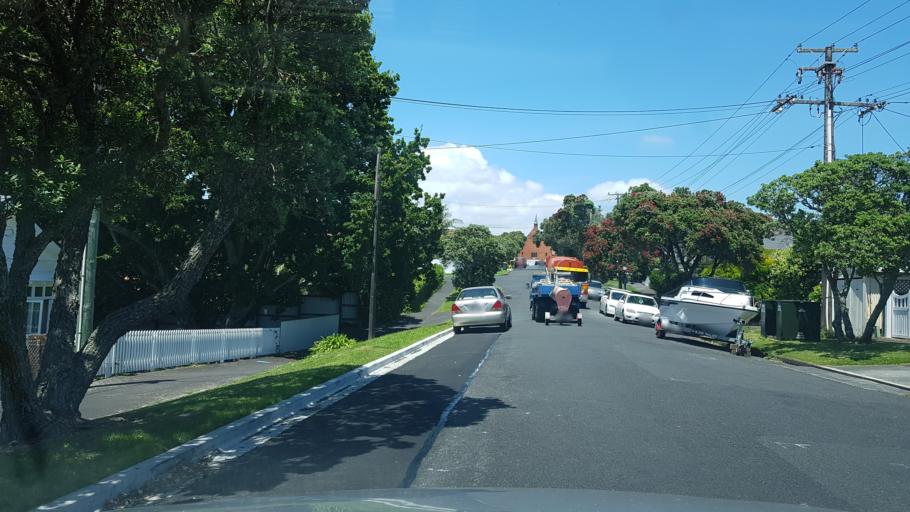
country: NZ
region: Auckland
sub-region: Auckland
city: Auckland
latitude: -36.8267
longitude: 174.7873
